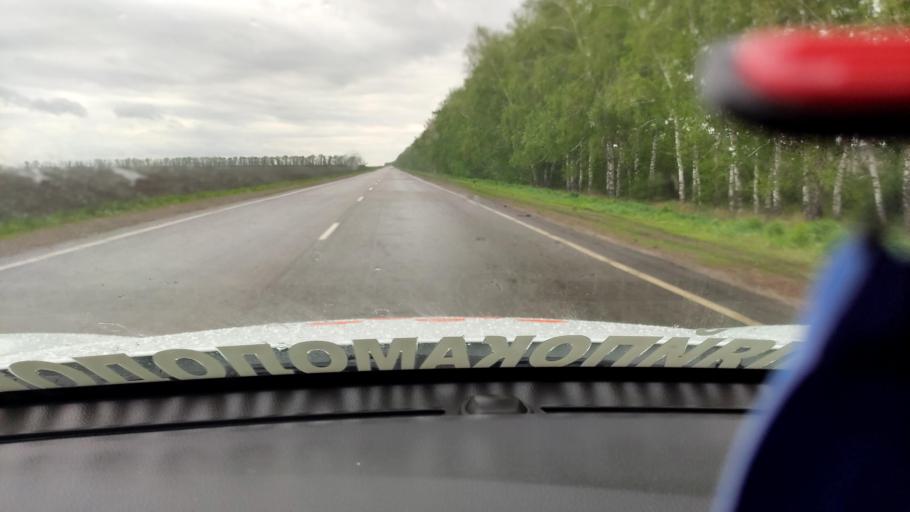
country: RU
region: Voronezj
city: Sredniy Ikorets
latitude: 51.0398
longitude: 39.6672
